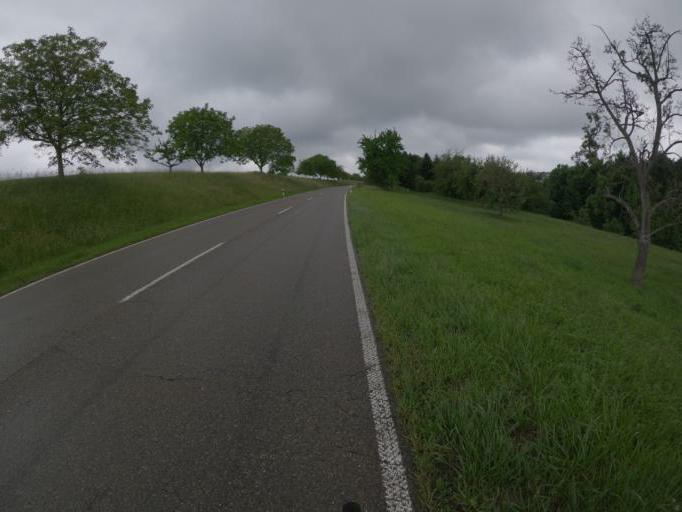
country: DE
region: Baden-Wuerttemberg
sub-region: Regierungsbezirk Stuttgart
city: Adelberg
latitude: 48.7549
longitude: 9.6054
